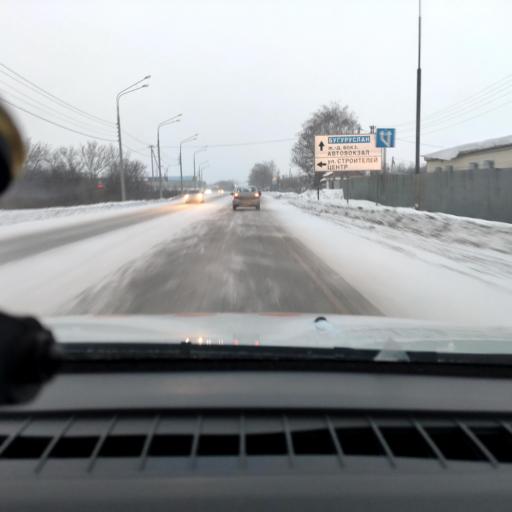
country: RU
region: Samara
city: Otradnyy
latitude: 53.3554
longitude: 51.3380
